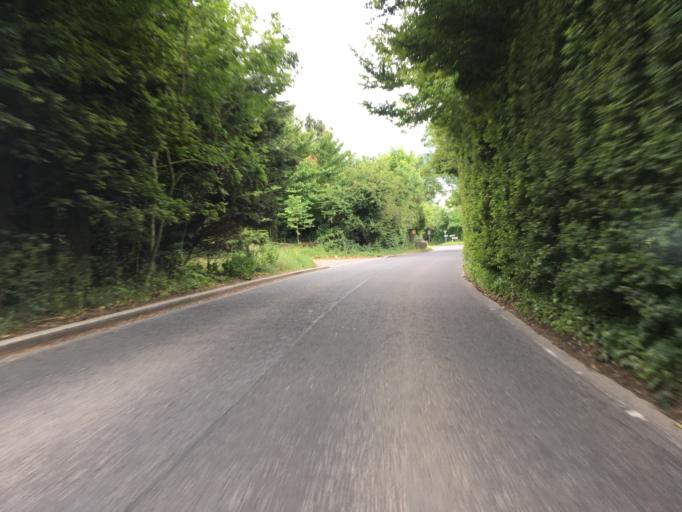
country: GB
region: England
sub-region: Wiltshire
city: Minety
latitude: 51.6528
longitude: -1.9390
